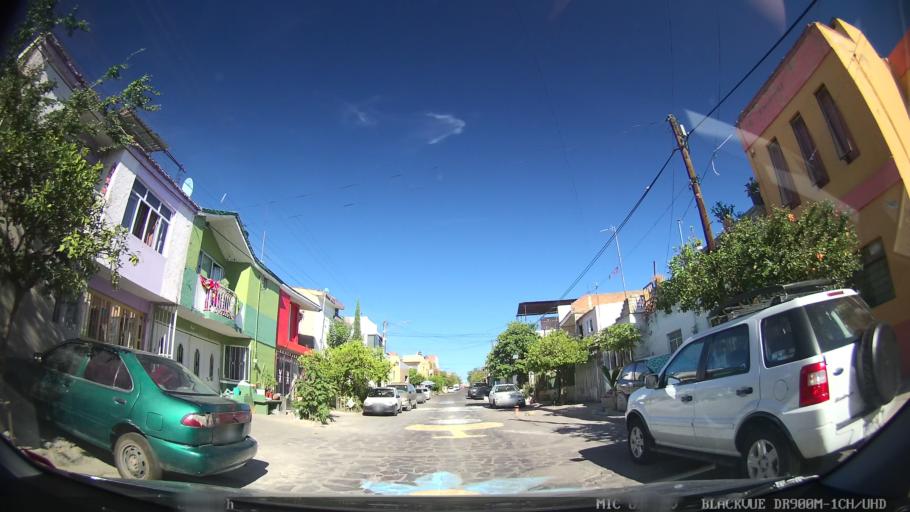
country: MX
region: Jalisco
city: Tlaquepaque
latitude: 20.6948
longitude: -103.2768
